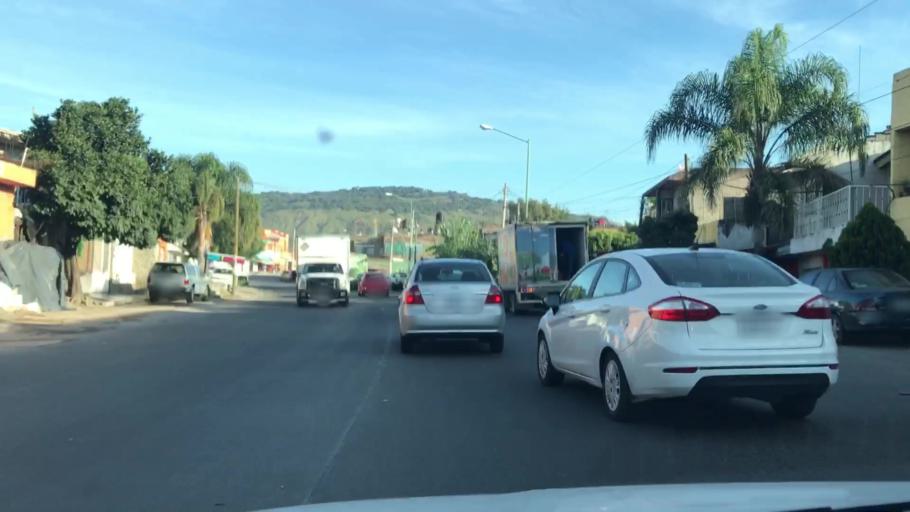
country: MX
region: Jalisco
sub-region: Tlajomulco de Zuniga
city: Palomar
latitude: 20.6319
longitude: -103.4603
